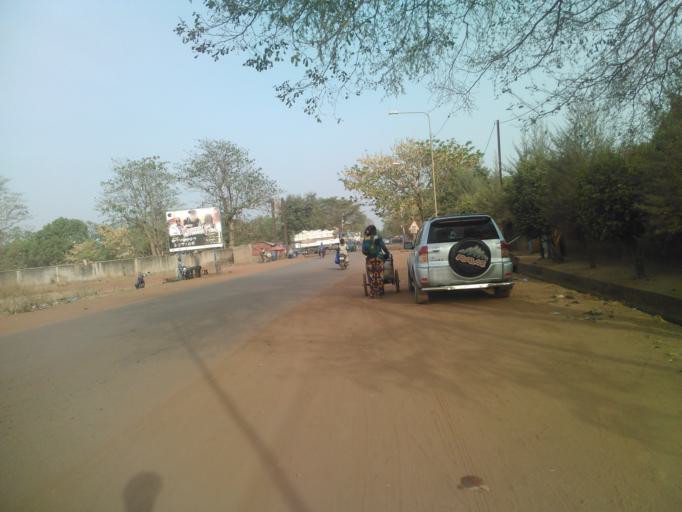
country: BF
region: High-Basins
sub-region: Province du Houet
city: Bobo-Dioulasso
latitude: 11.1742
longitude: -4.3084
